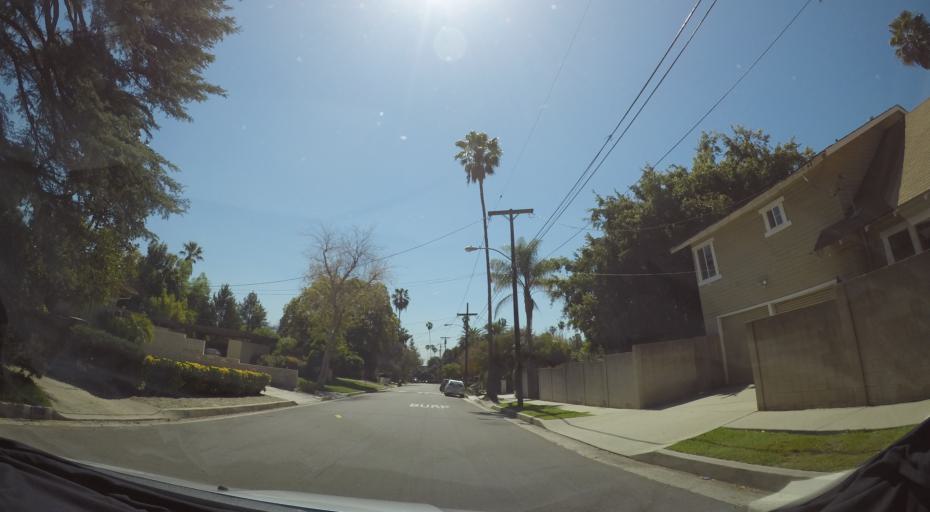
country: US
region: California
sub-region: Los Angeles County
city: Altadena
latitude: 34.1801
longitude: -118.1286
